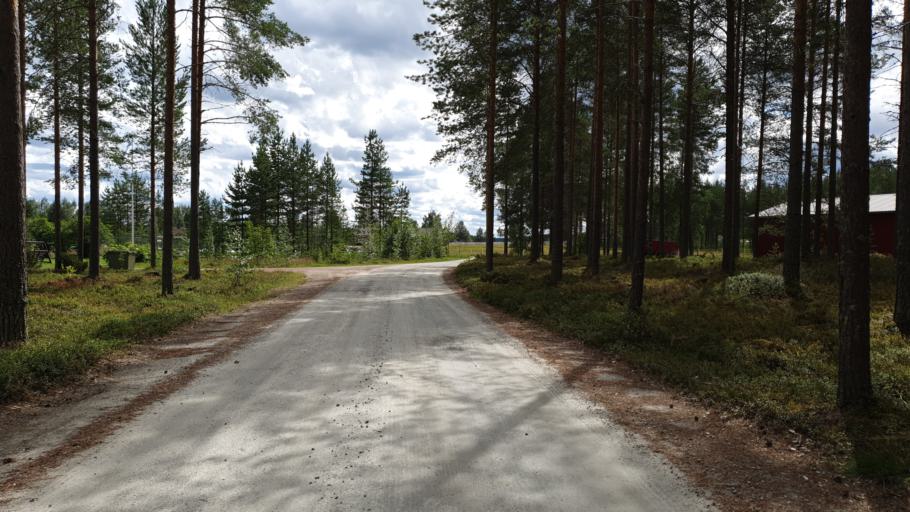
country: FI
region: Kainuu
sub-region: Kehys-Kainuu
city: Kuhmo
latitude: 64.3837
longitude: 29.8086
